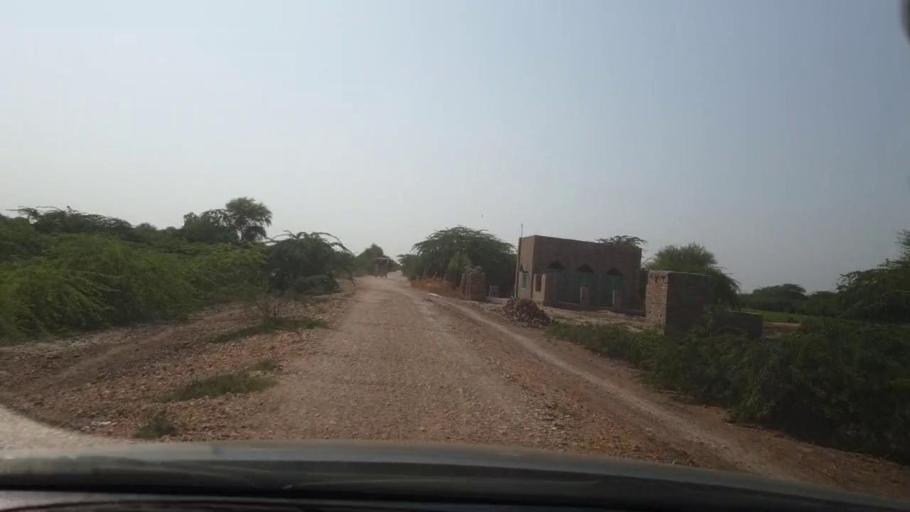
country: PK
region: Sindh
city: Naukot
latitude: 24.7959
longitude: 69.2247
